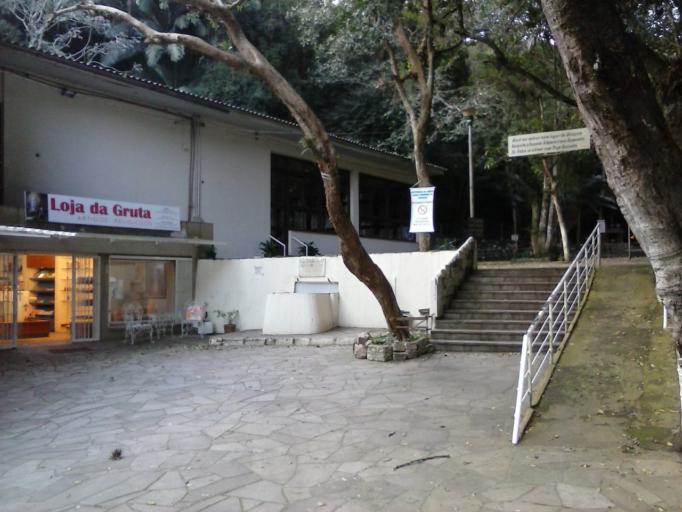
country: BR
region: Rio Grande do Sul
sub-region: Porto Alegre
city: Porto Alegre
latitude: -30.0844
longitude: -51.1886
